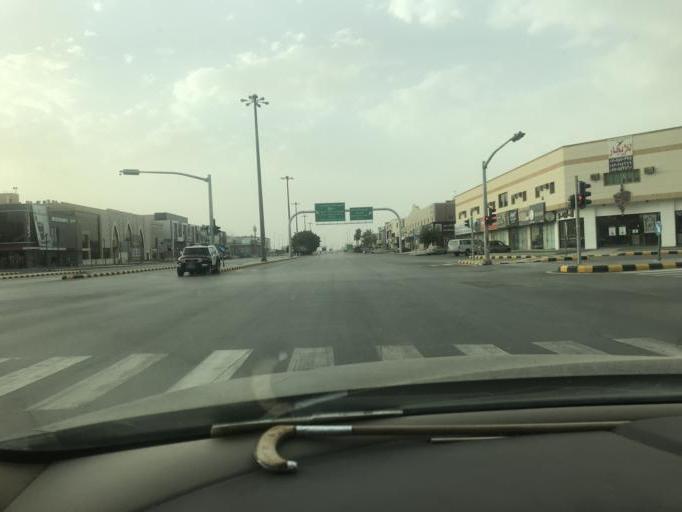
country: SA
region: Ar Riyad
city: Riyadh
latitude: 24.7936
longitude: 46.6567
